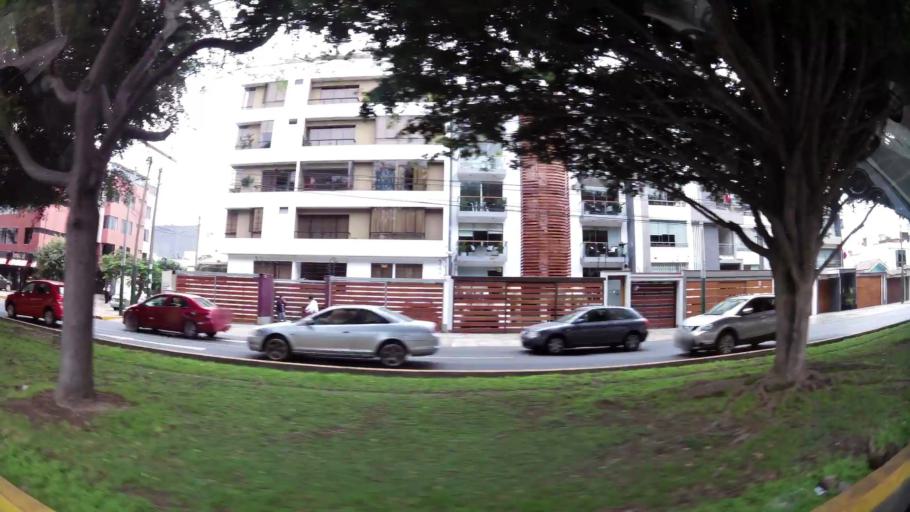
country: PE
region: Lima
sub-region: Lima
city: Surco
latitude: -12.1344
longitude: -77.0106
